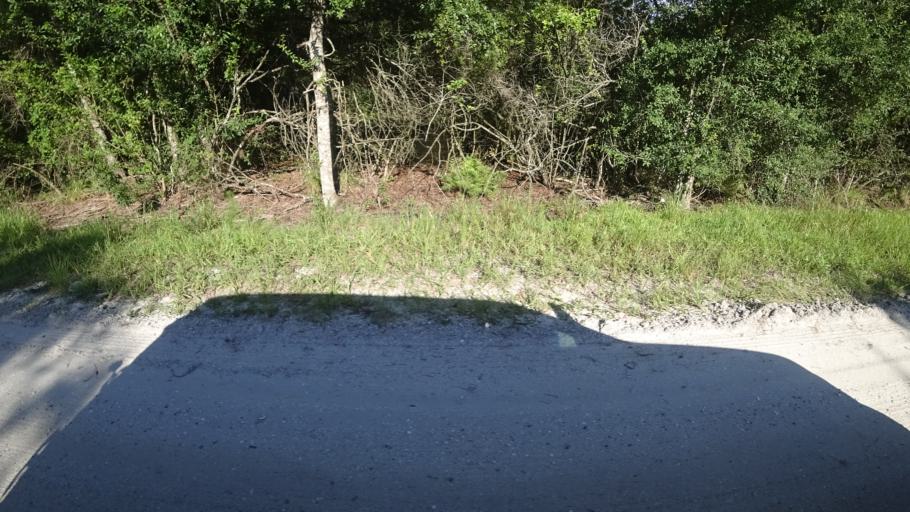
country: US
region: Florida
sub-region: Sarasota County
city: Lake Sarasota
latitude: 27.4134
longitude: -82.2520
